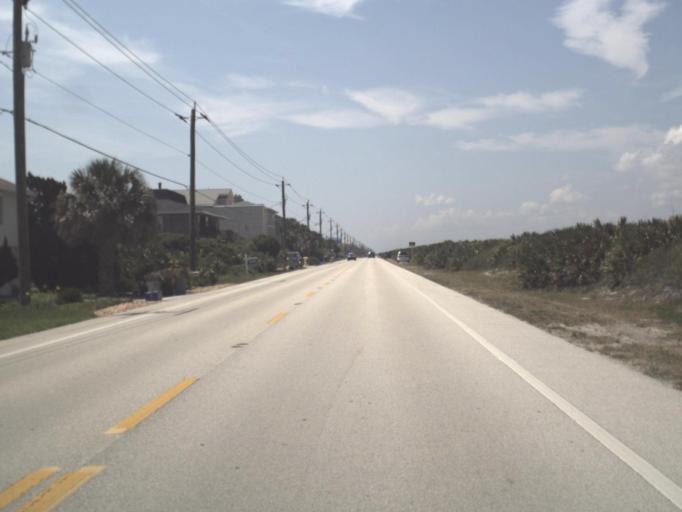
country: US
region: Florida
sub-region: Saint Johns County
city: Villano Beach
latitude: 30.0182
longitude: -81.3222
